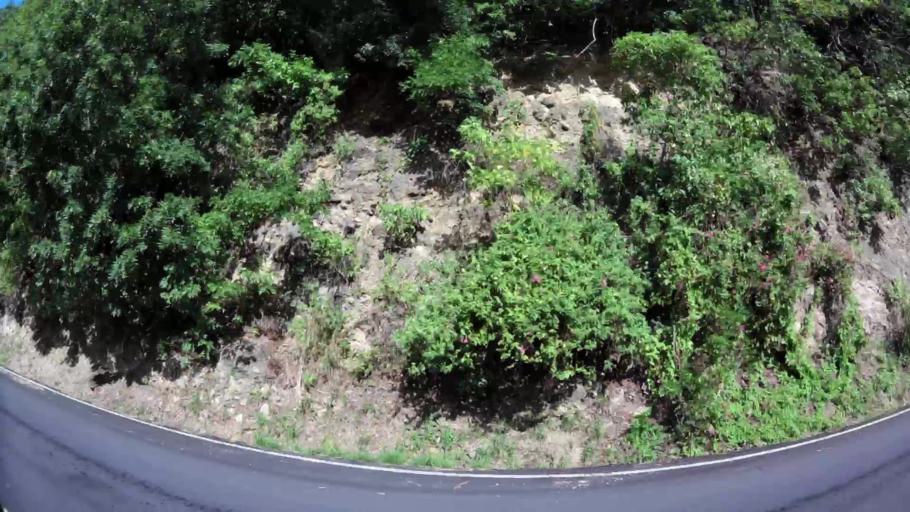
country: LC
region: Soufriere
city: Soufriere
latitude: 13.8653
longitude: -61.0522
